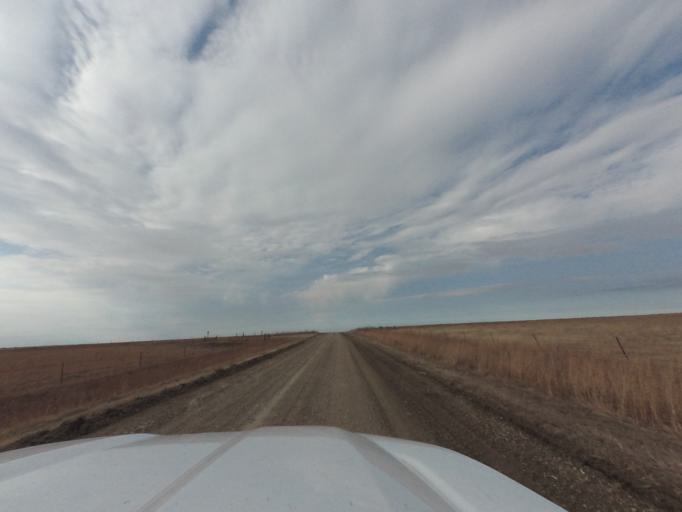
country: US
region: Kansas
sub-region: Chase County
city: Cottonwood Falls
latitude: 38.2172
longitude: -96.7111
